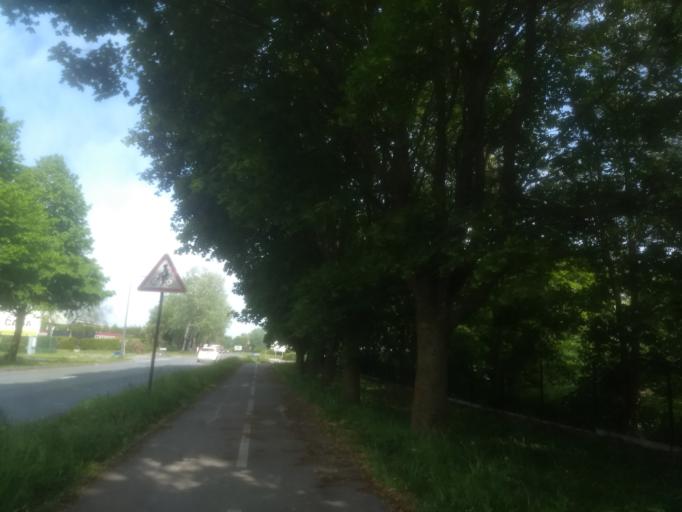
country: FR
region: Nord-Pas-de-Calais
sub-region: Departement du Pas-de-Calais
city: Saint-Laurent-Blangy
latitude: 50.2857
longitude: 2.8109
